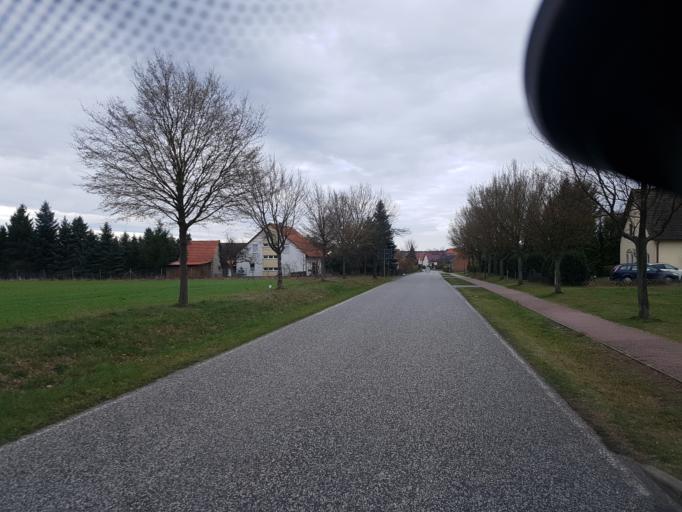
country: DE
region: Brandenburg
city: Mixdorf
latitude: 52.1985
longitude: 14.4073
